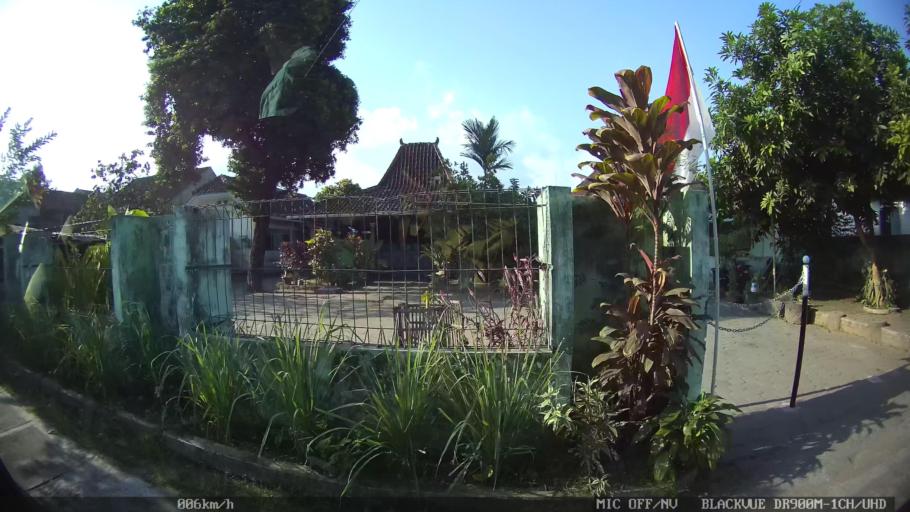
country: ID
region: Daerah Istimewa Yogyakarta
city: Yogyakarta
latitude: -7.8248
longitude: 110.3893
